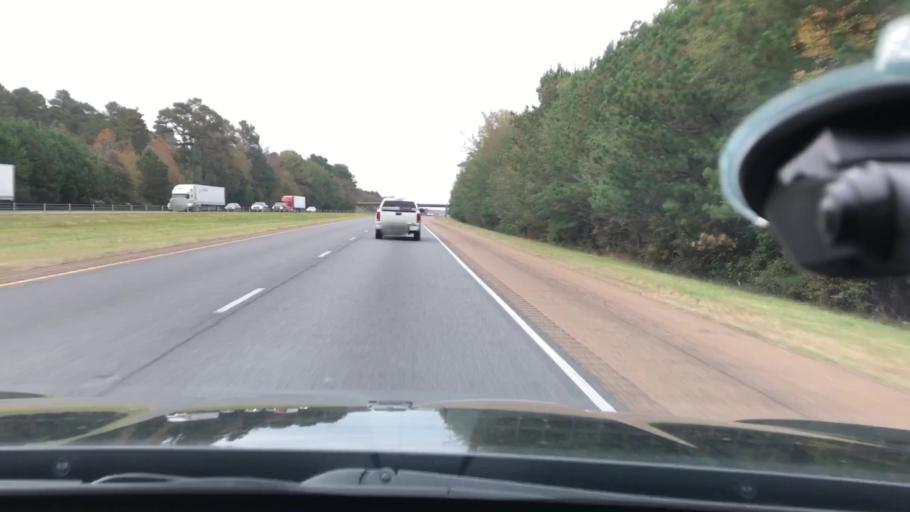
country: US
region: Arkansas
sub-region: Nevada County
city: Prescott
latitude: 33.8777
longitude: -93.3316
